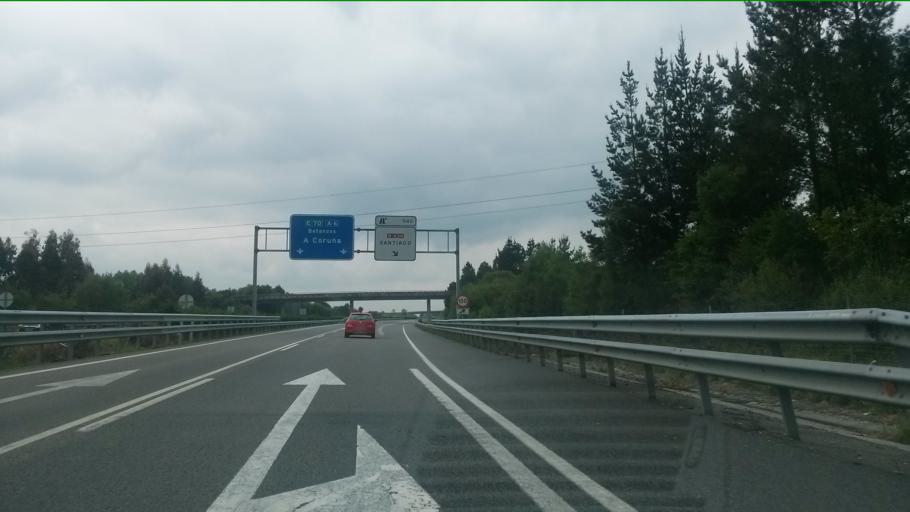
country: ES
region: Galicia
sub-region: Provincia de Lugo
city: Guitiriz
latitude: 43.1923
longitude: -7.9461
